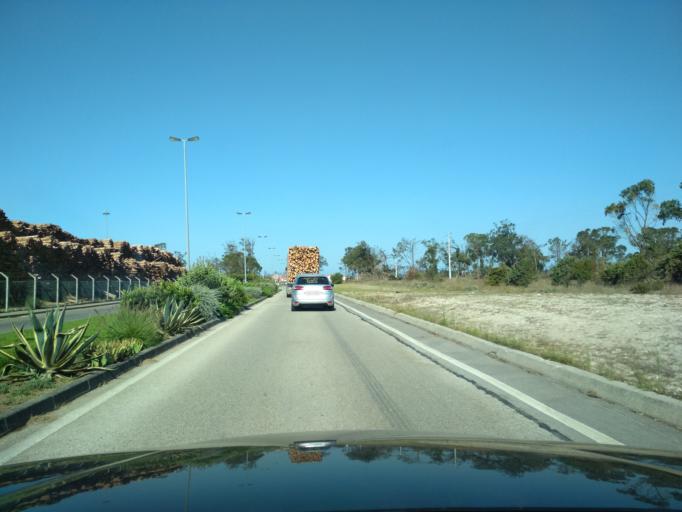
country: PT
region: Coimbra
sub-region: Figueira da Foz
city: Lavos
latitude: 40.0548
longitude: -8.8769
